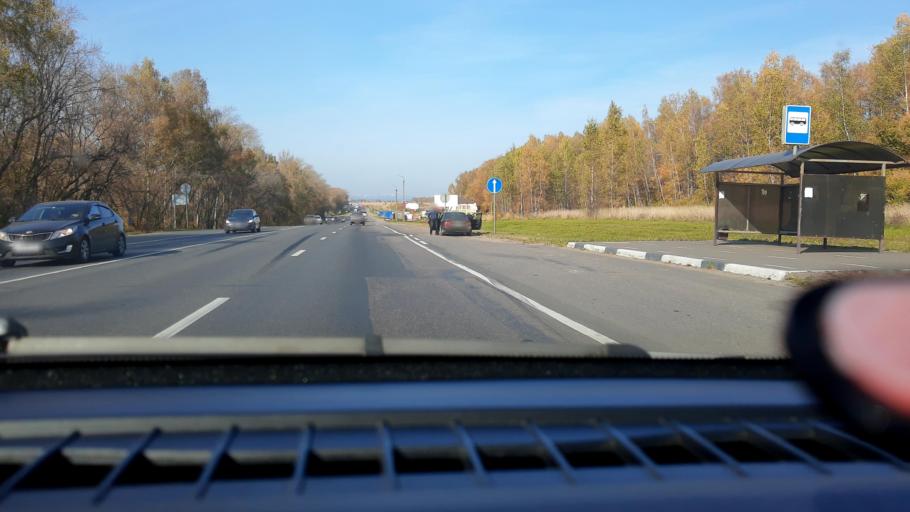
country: RU
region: Nizjnij Novgorod
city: Kstovo
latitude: 56.1151
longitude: 44.2788
